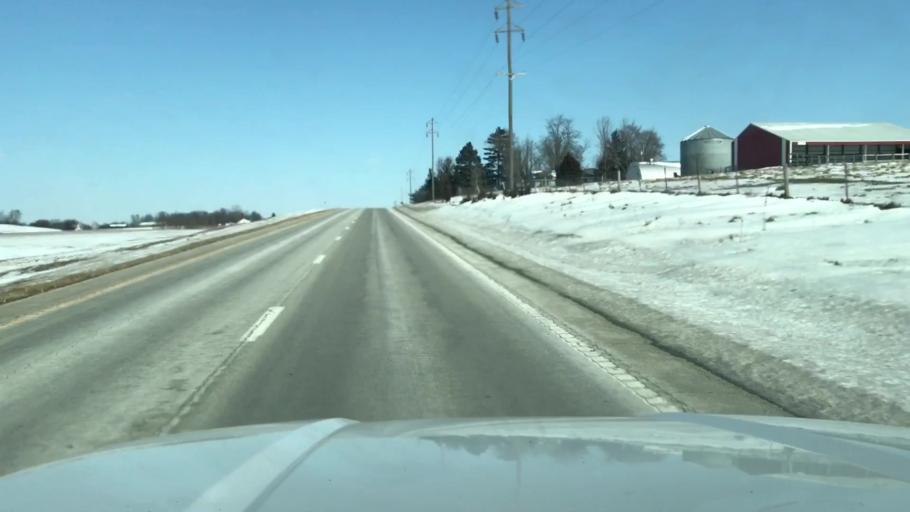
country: US
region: Missouri
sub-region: Nodaway County
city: Maryville
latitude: 40.1509
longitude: -94.8691
